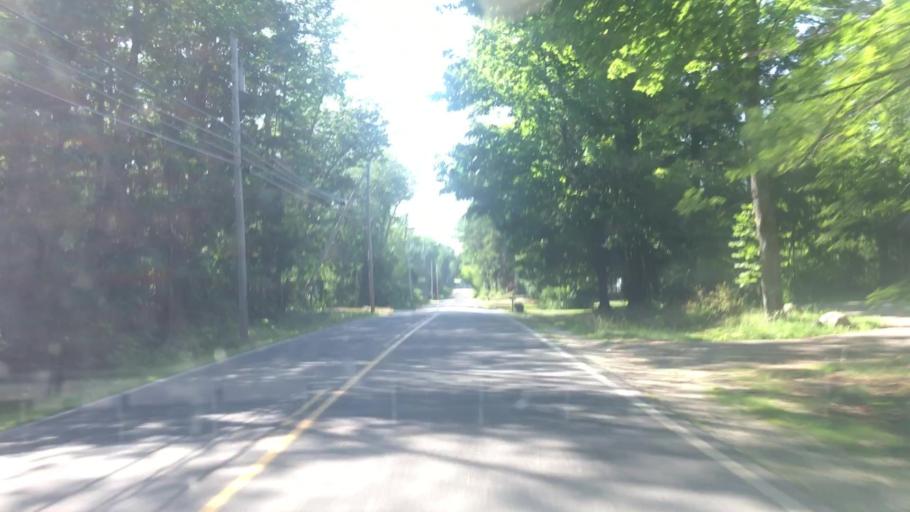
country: US
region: Maine
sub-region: York County
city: Hollis Center
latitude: 43.6374
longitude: -70.5779
